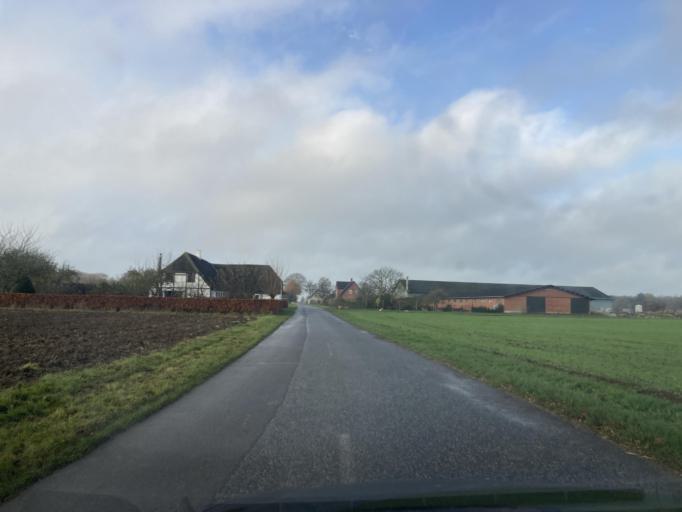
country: DK
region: Zealand
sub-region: Lolland Kommune
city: Rodby
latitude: 54.7910
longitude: 11.3618
